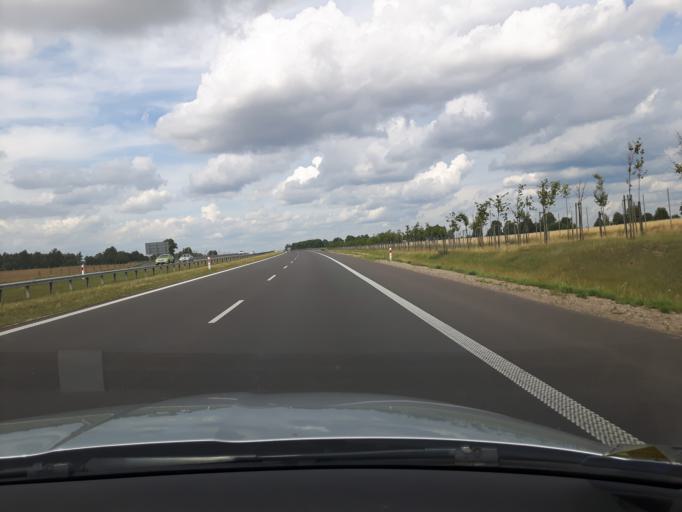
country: PL
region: Warmian-Masurian Voivodeship
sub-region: Powiat nidzicki
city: Nidzica
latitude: 53.2843
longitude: 20.4391
